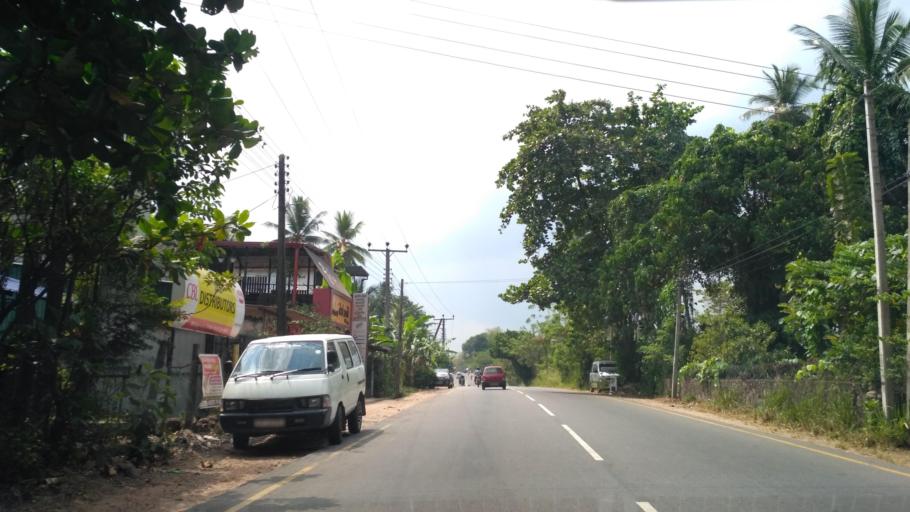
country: LK
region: North Western
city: Kuliyapitiya
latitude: 7.3266
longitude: 80.1157
